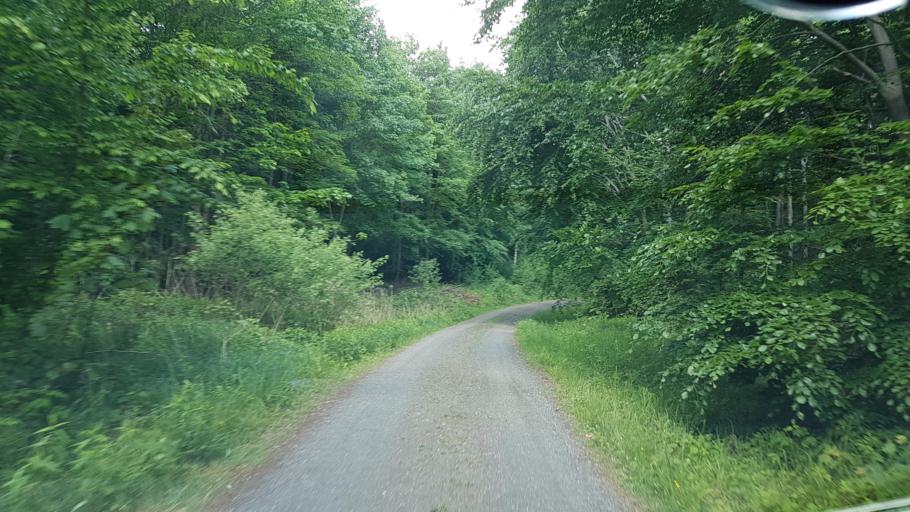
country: DE
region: Lower Saxony
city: Warberg
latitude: 52.1698
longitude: 10.8960
